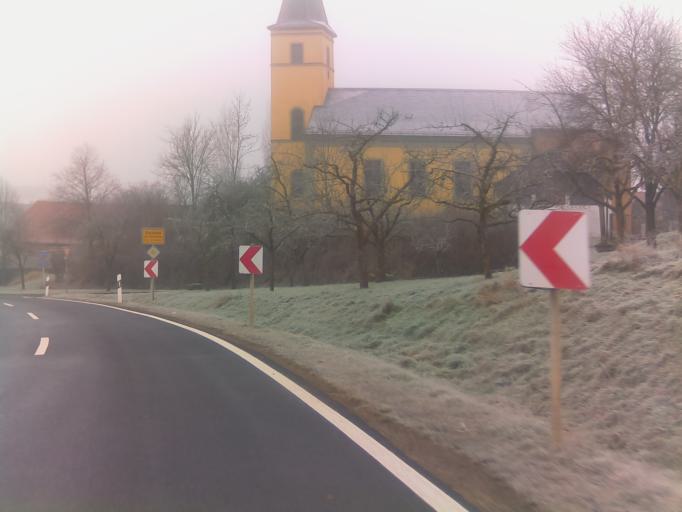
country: DE
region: Bavaria
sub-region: Regierungsbezirk Unterfranken
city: Dingolshausen
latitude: 49.9256
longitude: 10.4017
